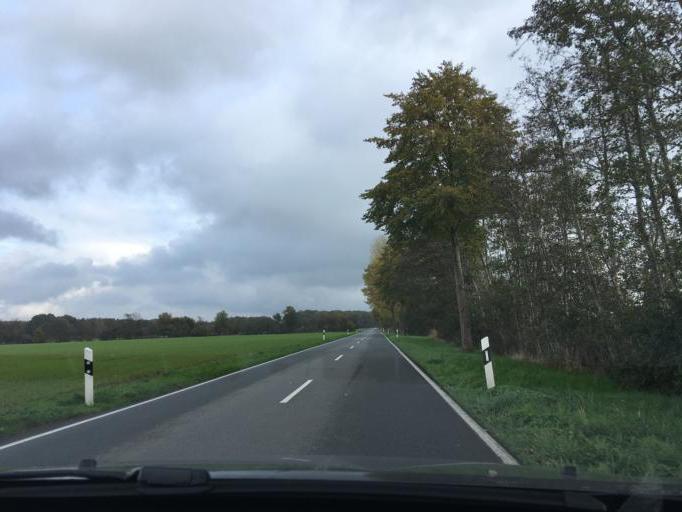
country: NL
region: Overijssel
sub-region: Gemeente Haaksbergen
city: Haaksbergen
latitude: 52.0687
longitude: 6.7317
